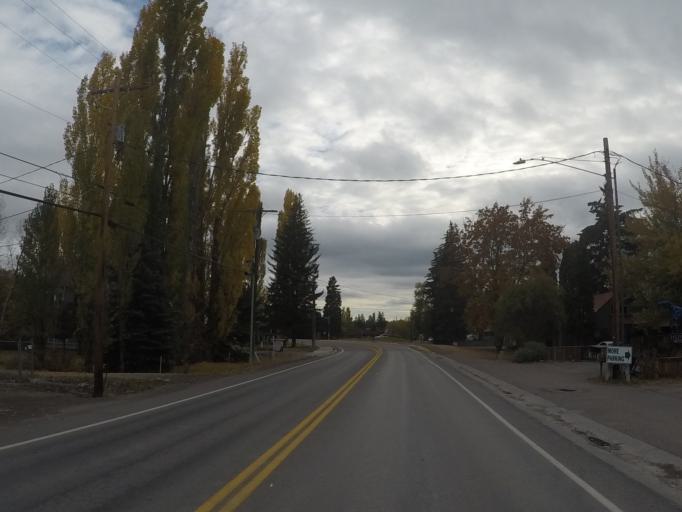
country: US
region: Montana
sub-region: Flathead County
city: Whitefish
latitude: 48.4173
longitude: -114.3411
